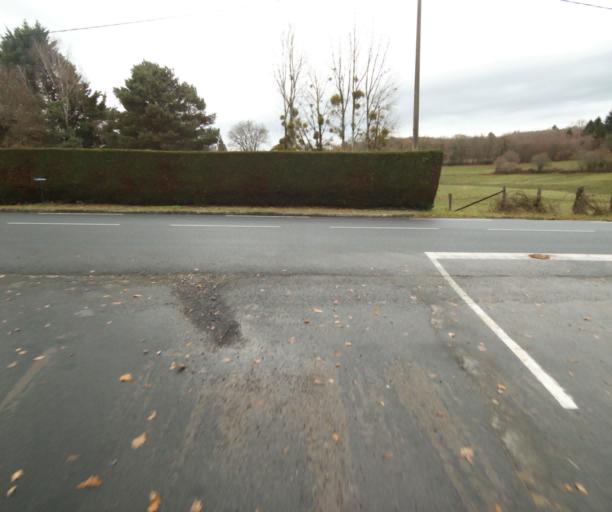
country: FR
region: Limousin
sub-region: Departement de la Correze
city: Saint-Mexant
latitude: 45.2773
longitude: 1.6235
